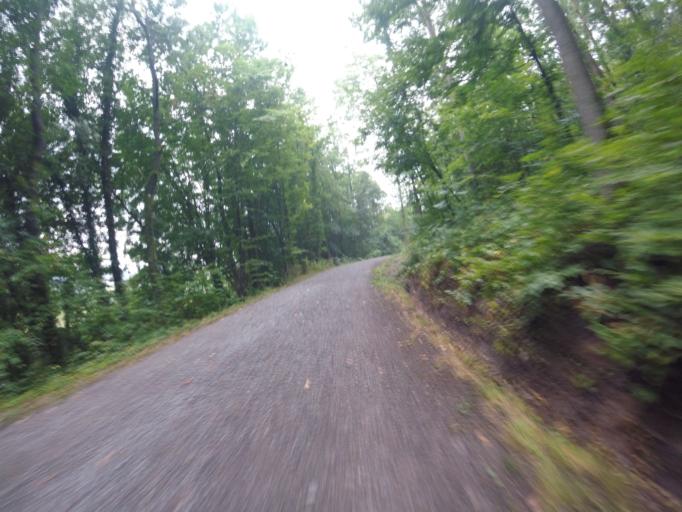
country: DE
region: Baden-Wuerttemberg
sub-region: Regierungsbezirk Stuttgart
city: Oppenweiler
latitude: 48.9832
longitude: 9.4372
